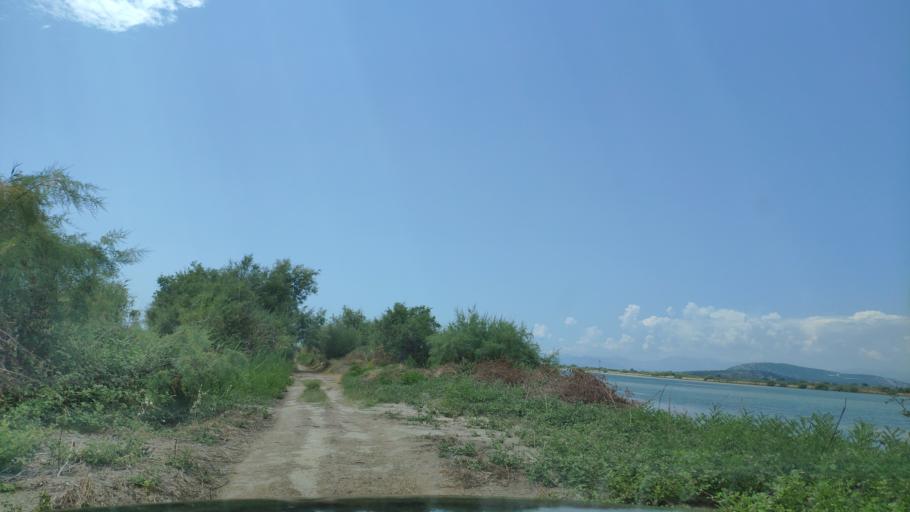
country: GR
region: West Greece
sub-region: Nomos Aitolias kai Akarnanias
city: Menidi
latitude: 39.0484
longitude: 21.0982
